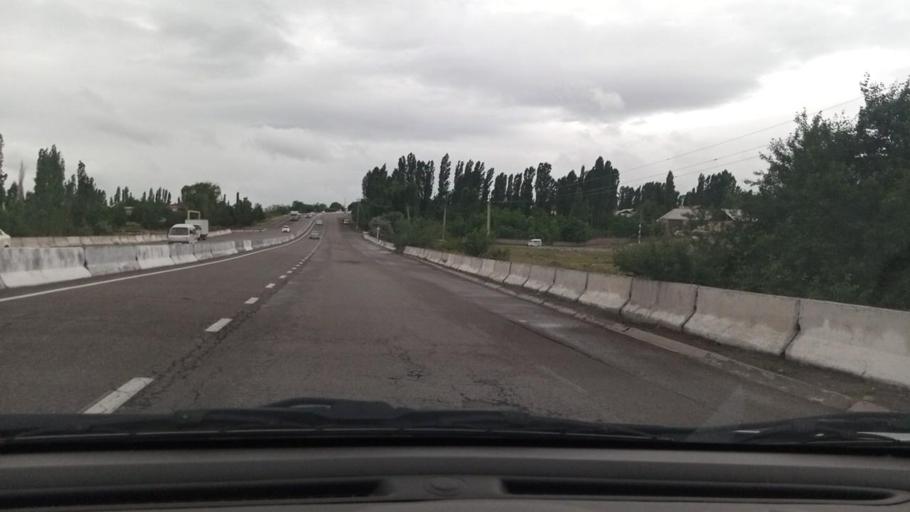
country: UZ
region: Toshkent
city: Angren
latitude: 40.9625
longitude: 69.9473
